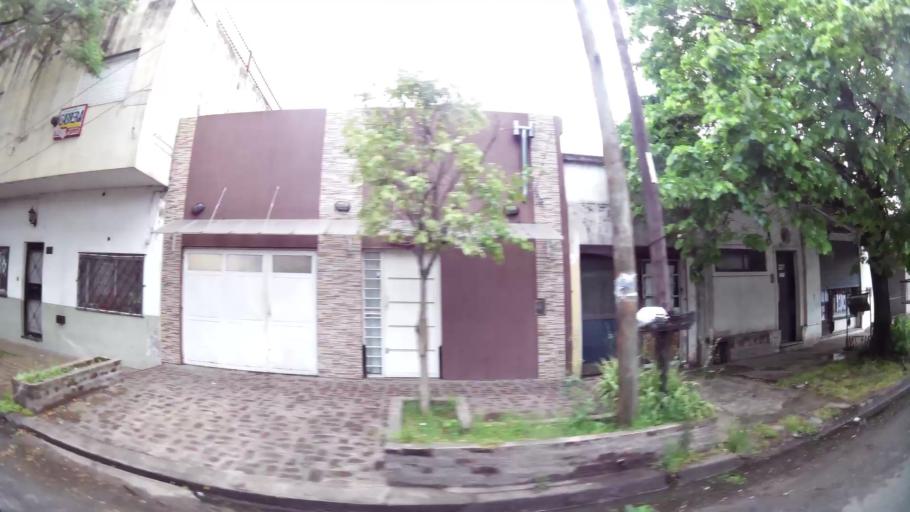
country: AR
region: Buenos Aires
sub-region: Partido de Lanus
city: Lanus
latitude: -34.7334
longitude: -58.3823
